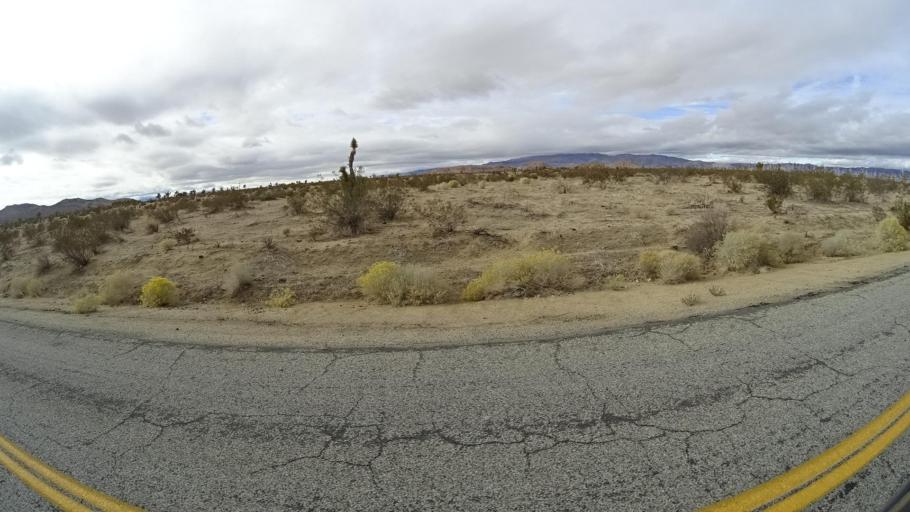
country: US
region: California
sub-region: Kern County
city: Mojave
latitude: 34.9573
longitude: -118.2127
